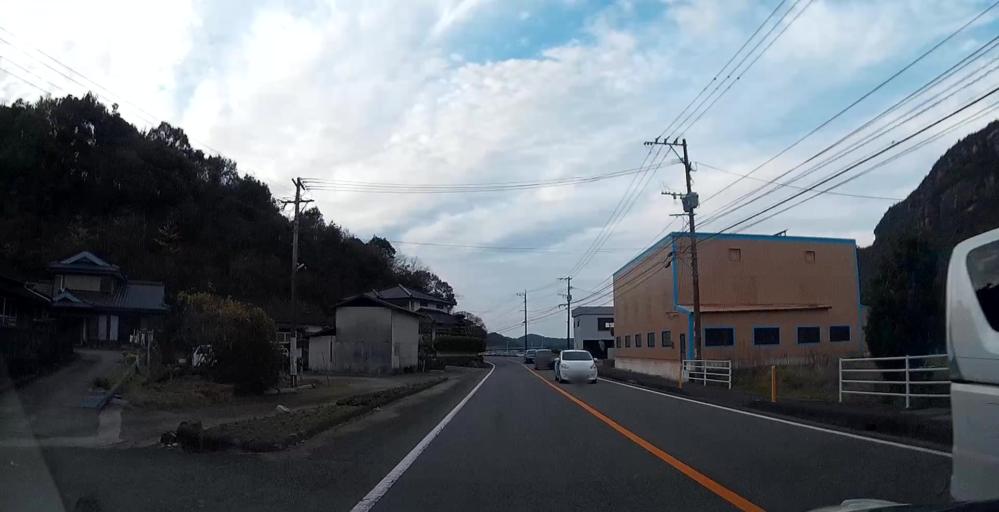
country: JP
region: Kumamoto
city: Yatsushiro
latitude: 32.4971
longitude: 130.4092
